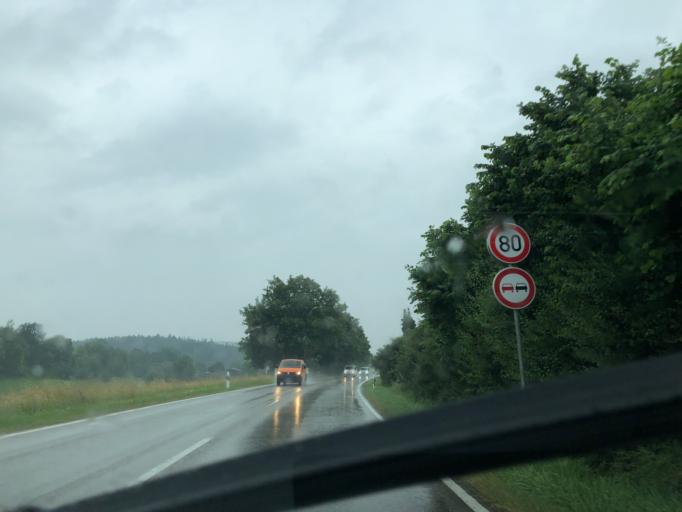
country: DE
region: Bavaria
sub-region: Upper Bavaria
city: Attenkirchen
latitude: 48.4936
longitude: 11.7626
